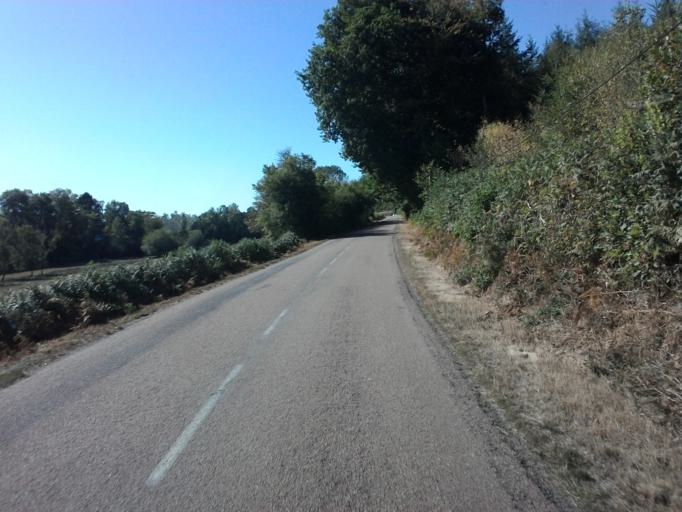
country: FR
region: Bourgogne
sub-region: Departement de la Nievre
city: Lormes
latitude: 47.2732
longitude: 3.9794
